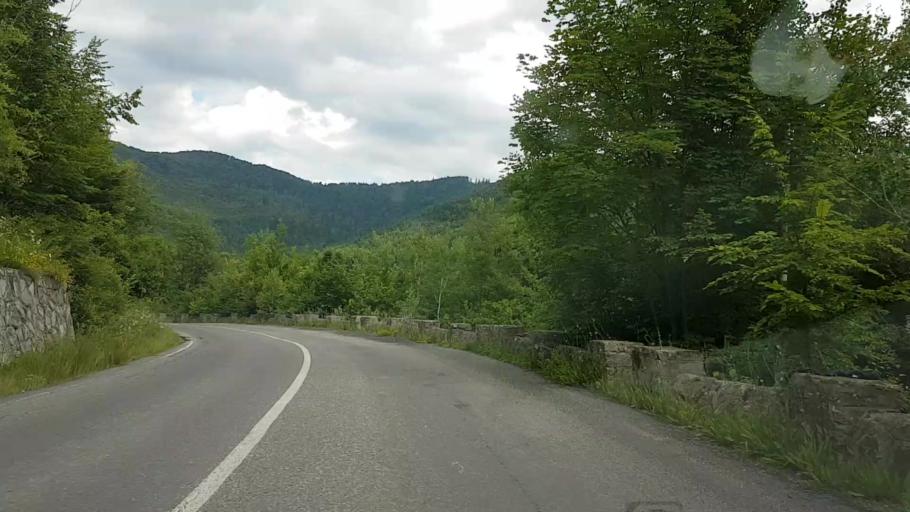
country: RO
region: Neamt
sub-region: Comuna Bicaz
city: Dodeni
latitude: 46.9888
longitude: 26.1099
